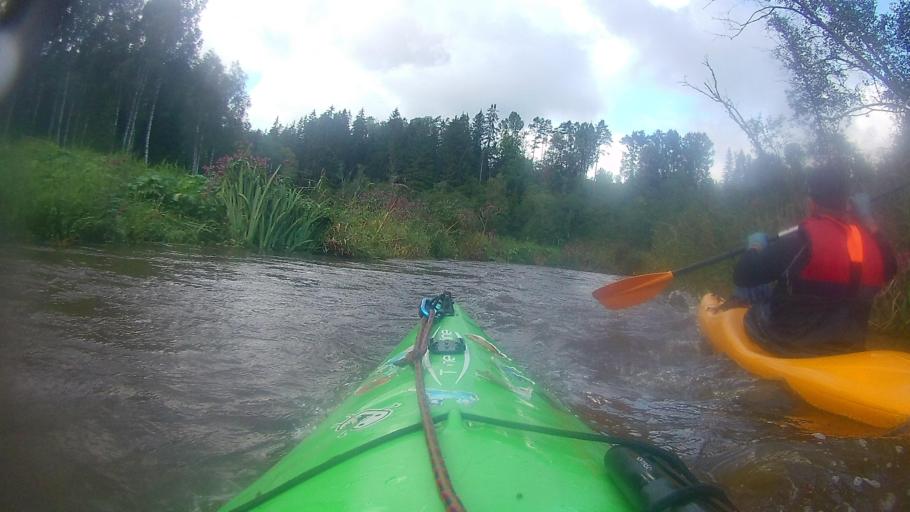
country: LV
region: Talsu Rajons
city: Sabile
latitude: 57.0010
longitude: 22.5961
